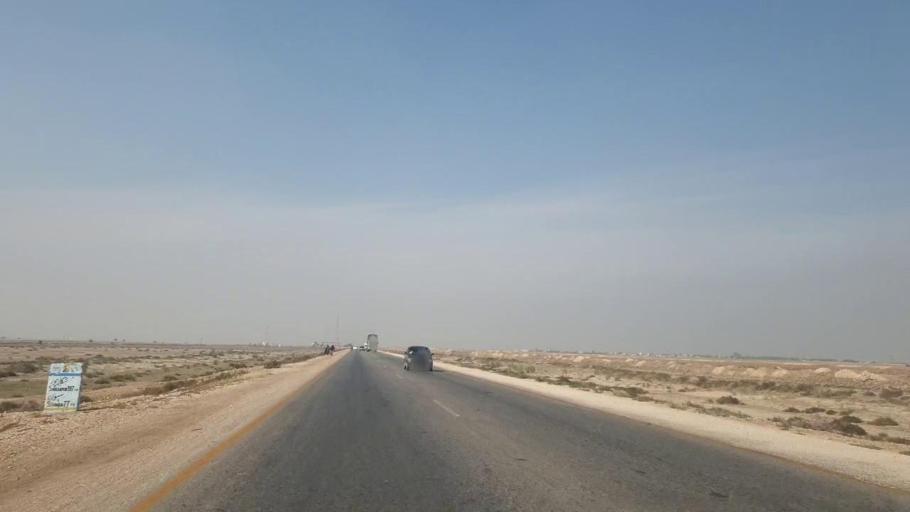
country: PK
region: Sindh
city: Sann
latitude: 25.8915
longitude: 68.2395
